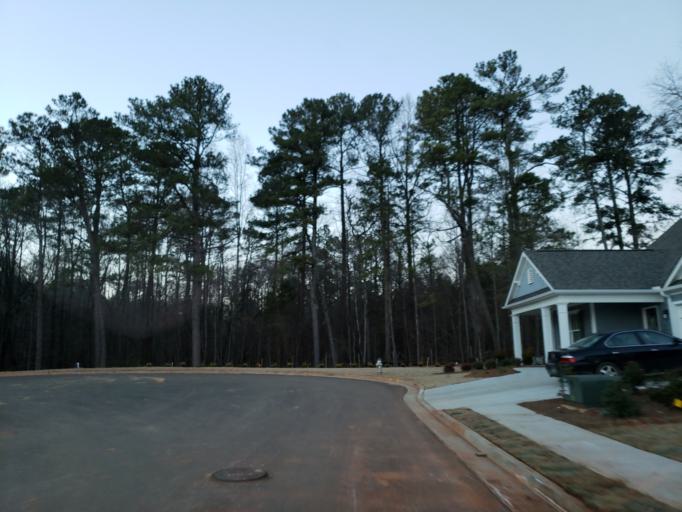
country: US
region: Georgia
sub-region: Cobb County
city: Powder Springs
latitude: 33.9357
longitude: -84.7027
